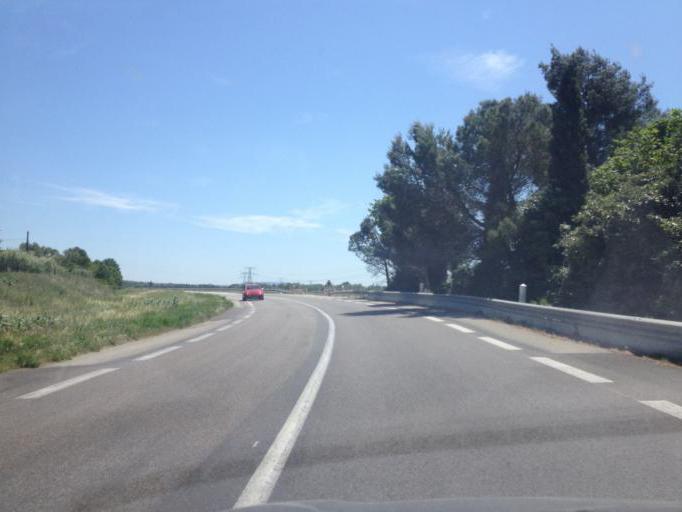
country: FR
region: Provence-Alpes-Cote d'Azur
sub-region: Departement du Vaucluse
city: Cavaillon
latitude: 43.8380
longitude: 5.0161
